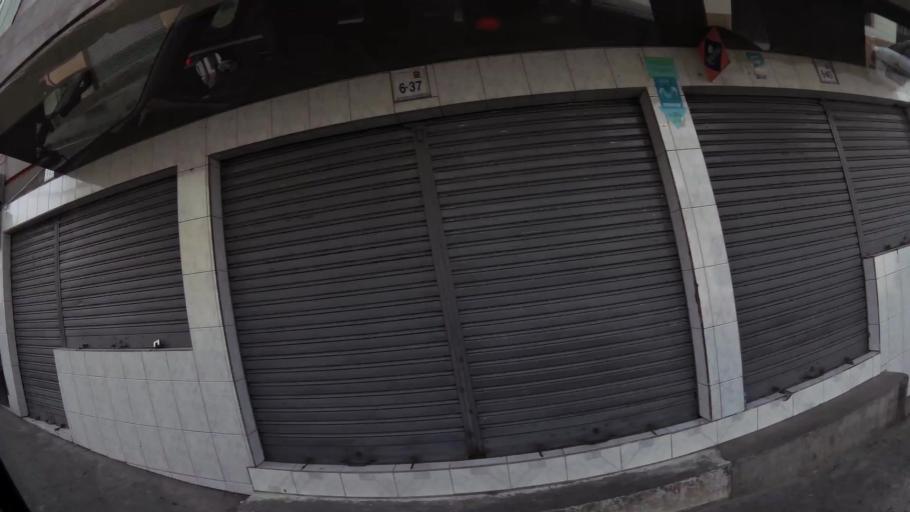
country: EC
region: Cotopaxi
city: Latacunga
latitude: -0.9280
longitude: -78.6106
